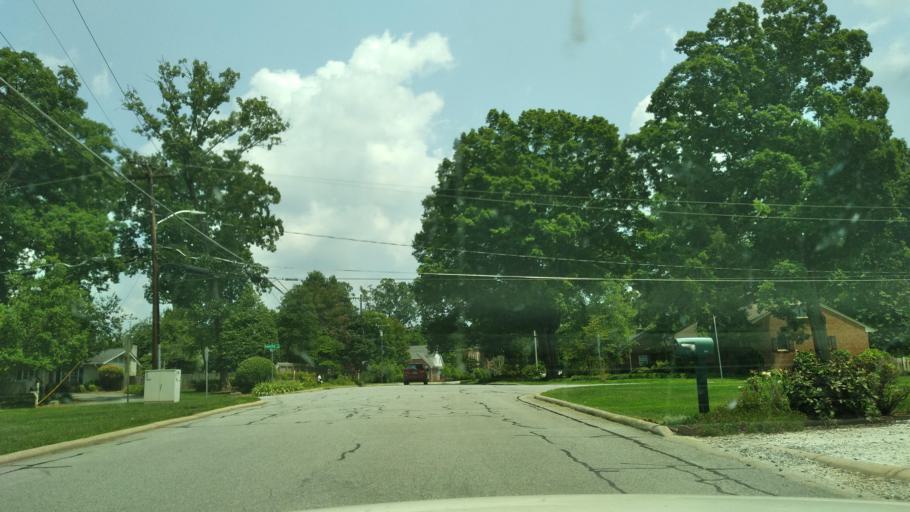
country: US
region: North Carolina
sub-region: Guilford County
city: Greensboro
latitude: 36.1206
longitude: -79.8506
